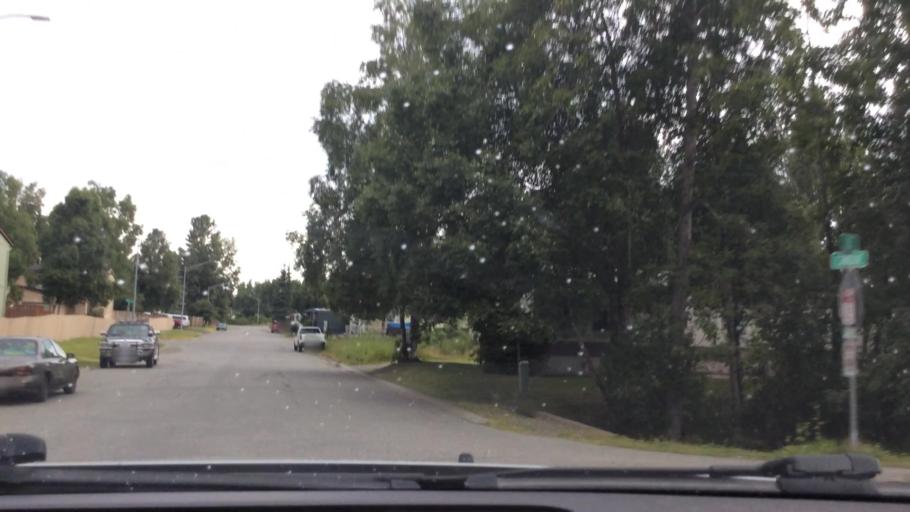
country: US
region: Alaska
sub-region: Anchorage Municipality
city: Anchorage
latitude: 61.1891
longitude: -149.7758
